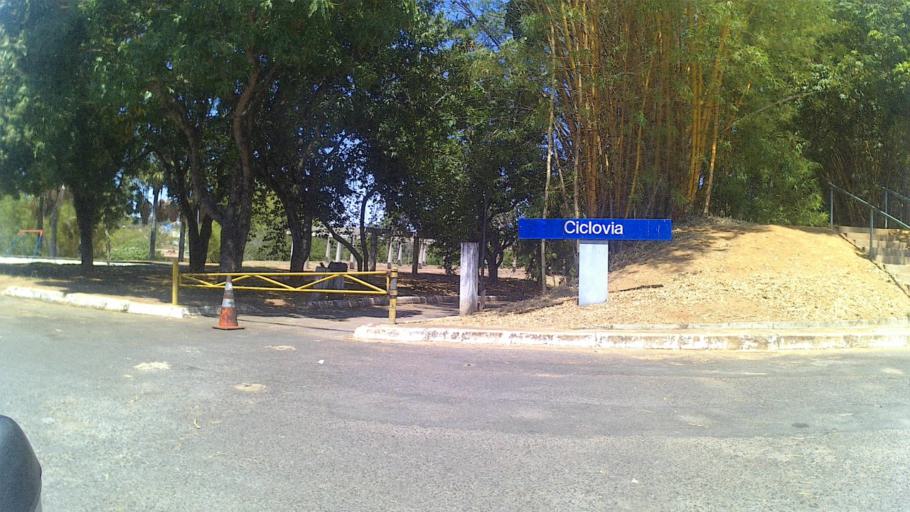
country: BR
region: Federal District
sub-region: Brasilia
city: Brasilia
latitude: -15.7286
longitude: -47.8932
